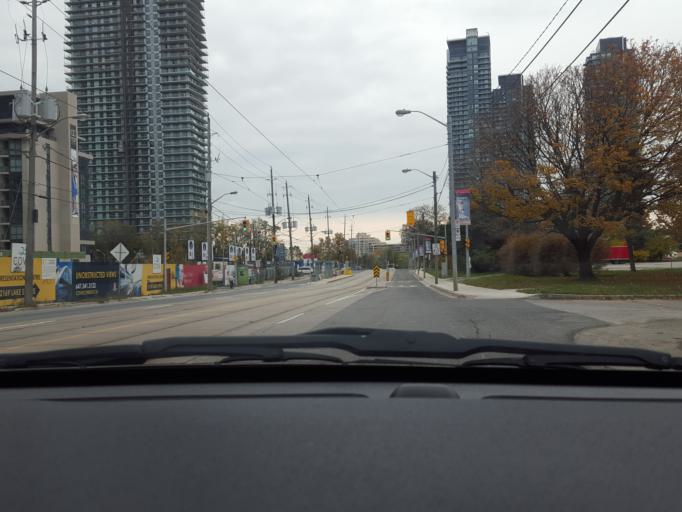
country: CA
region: Ontario
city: Etobicoke
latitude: 43.6265
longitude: -79.4795
